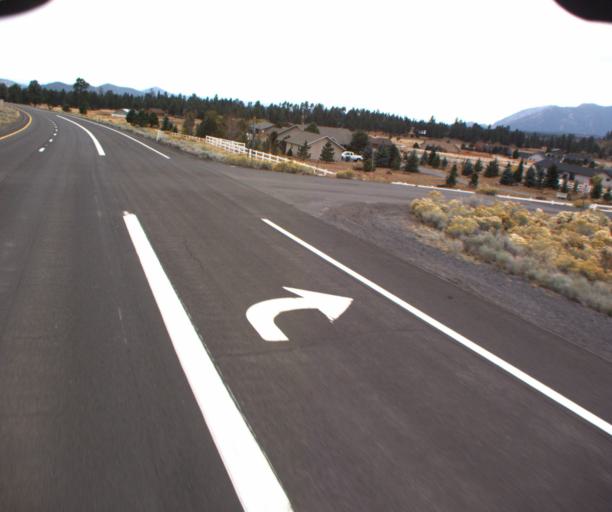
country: US
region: Arizona
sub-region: Coconino County
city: Flagstaff
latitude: 35.3449
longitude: -111.5617
